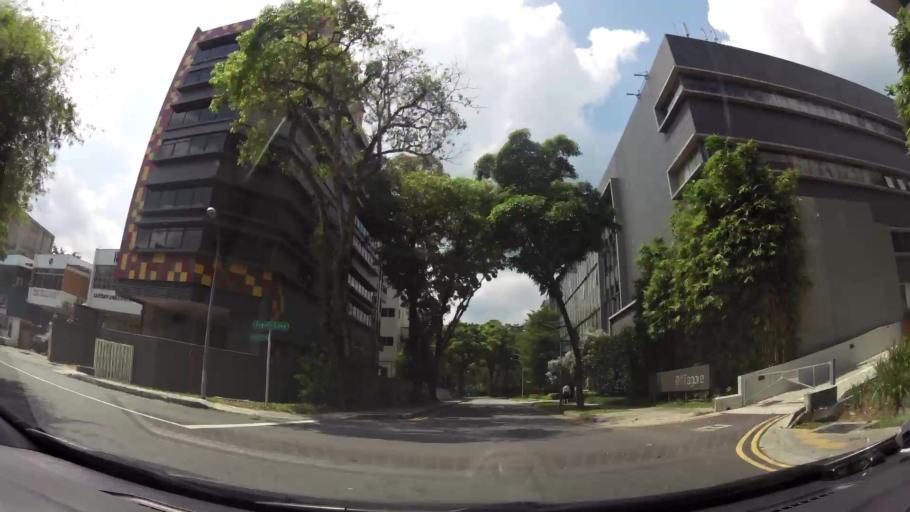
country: SG
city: Singapore
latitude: 1.3836
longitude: 103.8270
